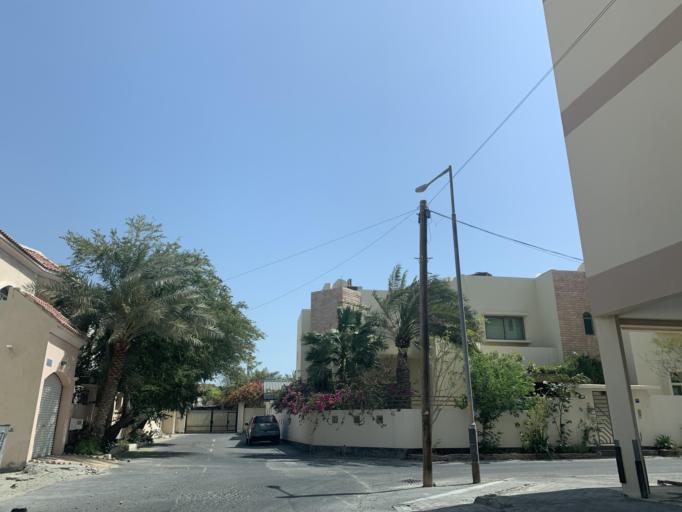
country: BH
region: Manama
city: Manama
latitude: 26.2084
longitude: 50.5786
